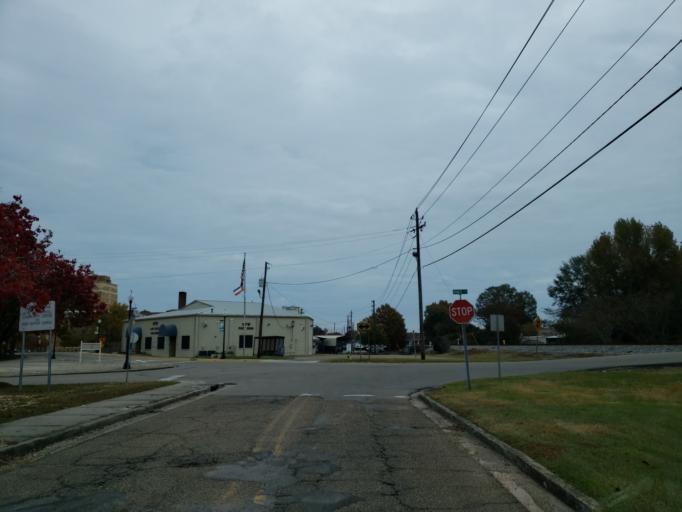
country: US
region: Mississippi
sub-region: Forrest County
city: Hattiesburg
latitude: 31.3236
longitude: -89.2919
